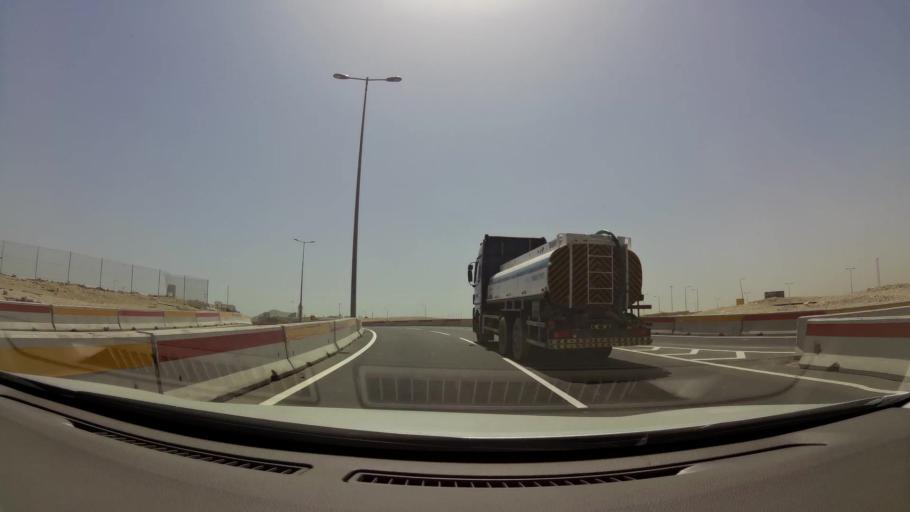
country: QA
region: Baladiyat Umm Salal
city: Umm Salal Muhammad
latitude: 25.3966
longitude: 51.4967
